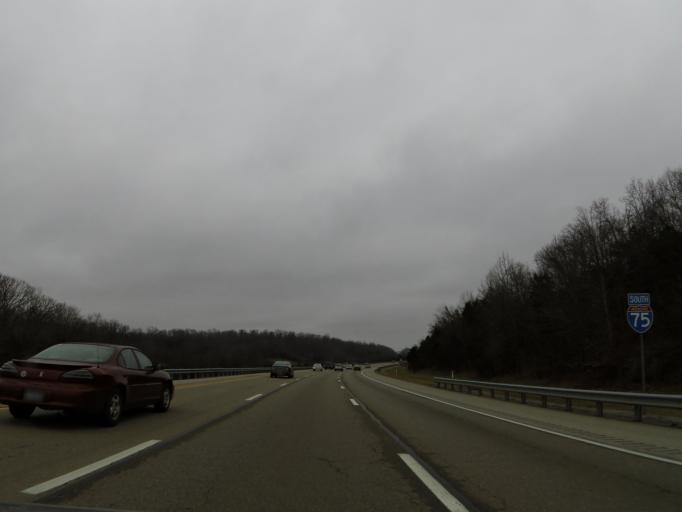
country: US
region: Kentucky
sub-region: Grant County
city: Williamstown
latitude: 38.4821
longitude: -84.5818
